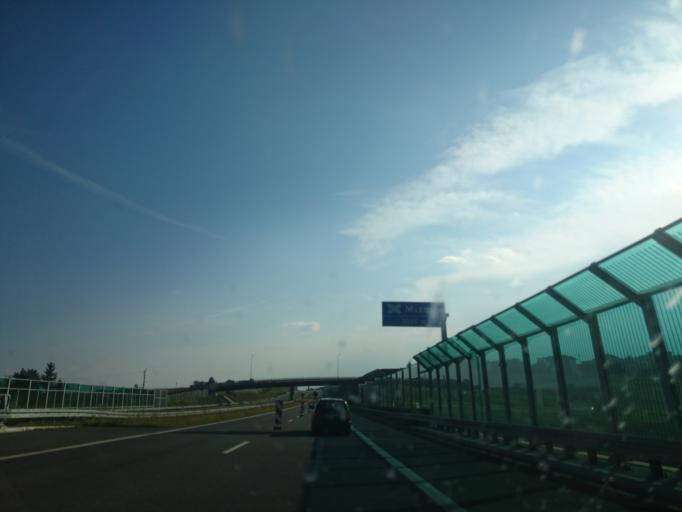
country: PL
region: Silesian Voivodeship
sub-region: Powiat rybnicki
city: Swierklany Dolne
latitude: 49.9972
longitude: 18.5741
